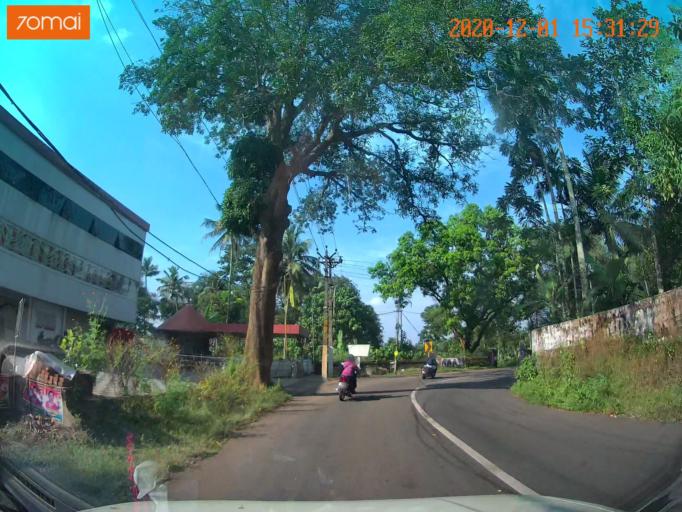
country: IN
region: Kerala
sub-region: Ernakulam
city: Muvattupuzha
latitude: 9.9701
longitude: 76.5693
